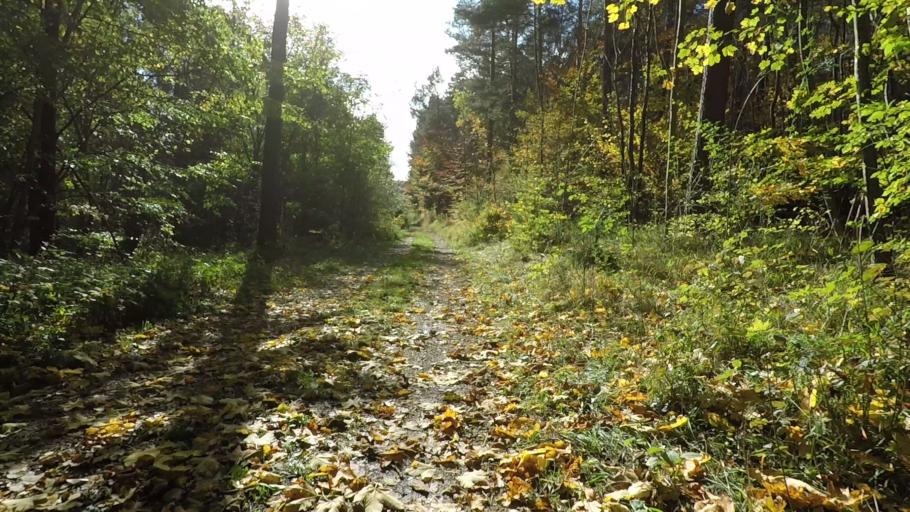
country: DE
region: Baden-Wuerttemberg
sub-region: Tuebingen Region
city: Pfullingen
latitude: 48.4336
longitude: 9.2316
